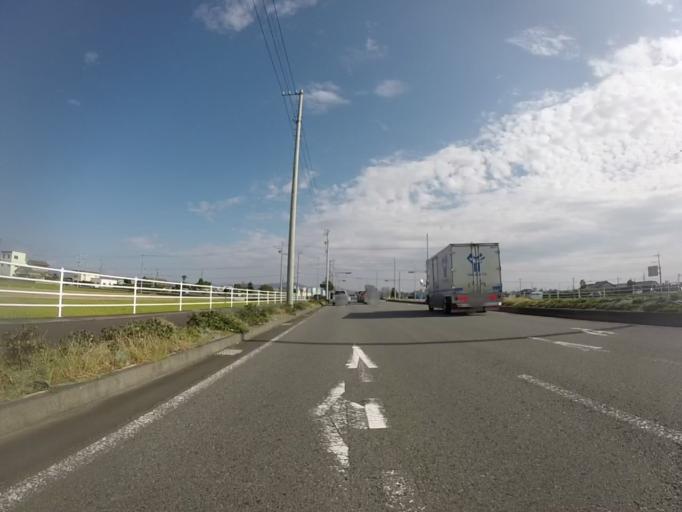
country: JP
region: Shizuoka
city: Fujieda
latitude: 34.8197
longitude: 138.2592
